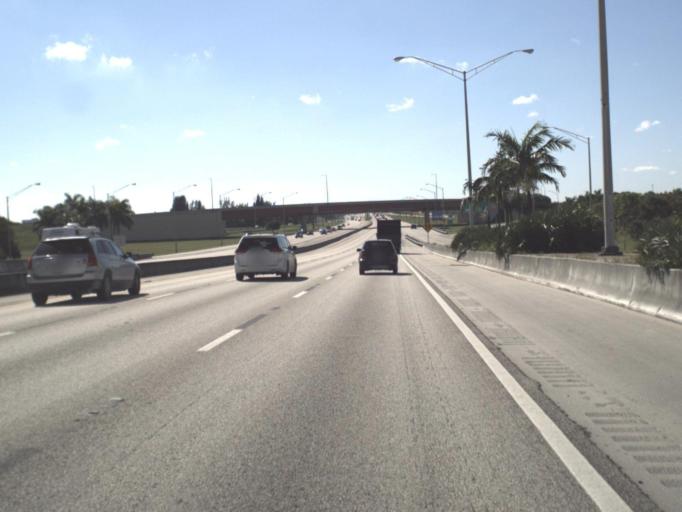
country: US
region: Florida
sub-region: Miami-Dade County
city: Sweetwater
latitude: 25.7802
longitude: -80.3861
